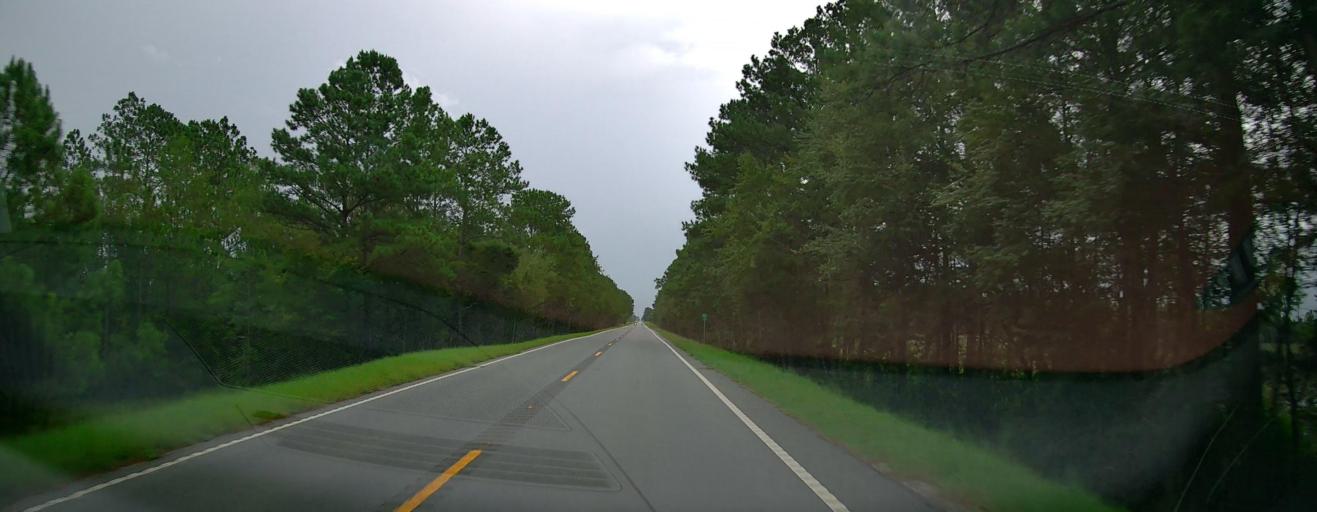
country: US
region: Georgia
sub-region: Brantley County
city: Nahunta
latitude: 31.3479
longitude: -82.0182
